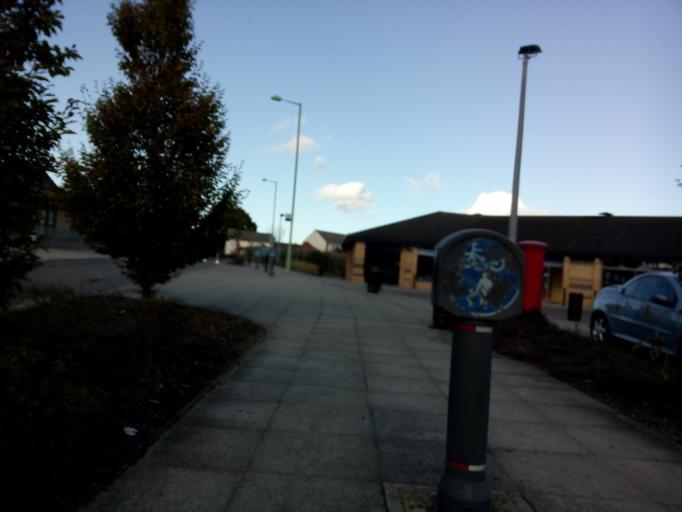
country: GB
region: England
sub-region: Suffolk
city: Kesgrave
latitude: 52.0552
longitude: 1.2168
